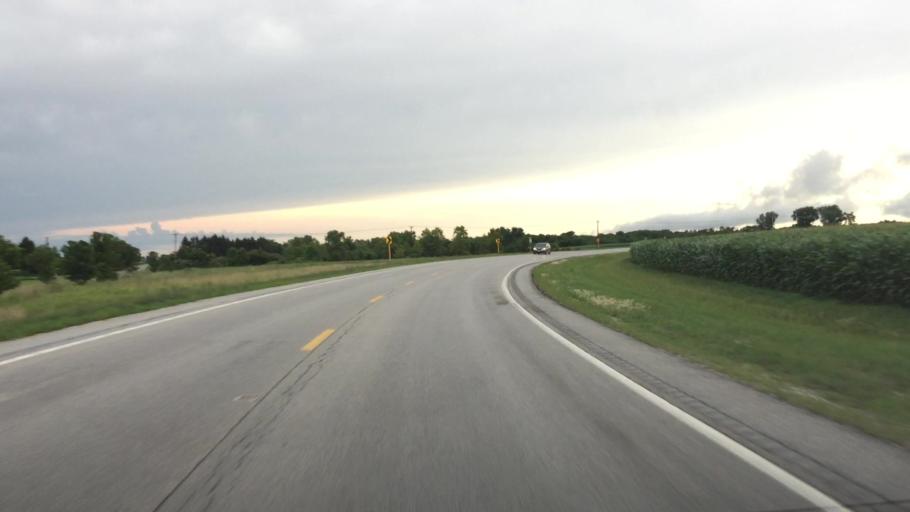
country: US
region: Illinois
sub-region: Hancock County
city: Hamilton
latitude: 40.3655
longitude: -91.3423
